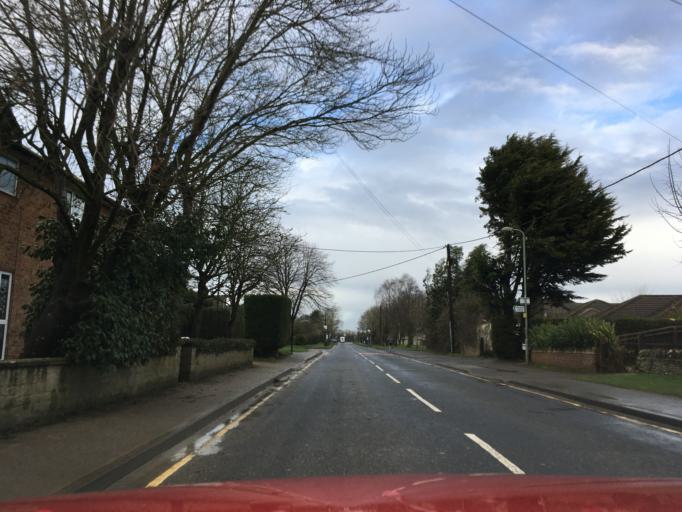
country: GB
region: England
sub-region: Oxfordshire
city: Eynsham
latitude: 51.7839
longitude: -1.3823
